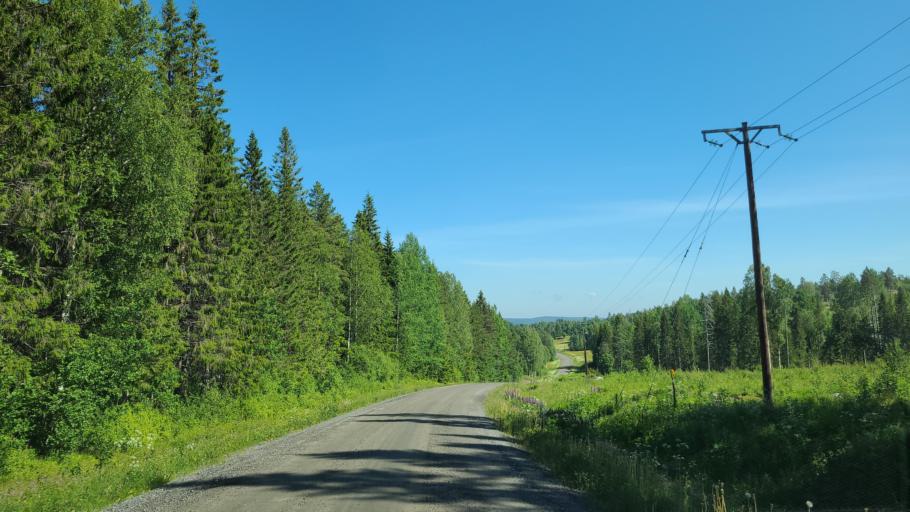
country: SE
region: Vaesterbotten
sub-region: Bjurholms Kommun
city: Bjurholm
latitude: 63.6428
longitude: 19.1651
